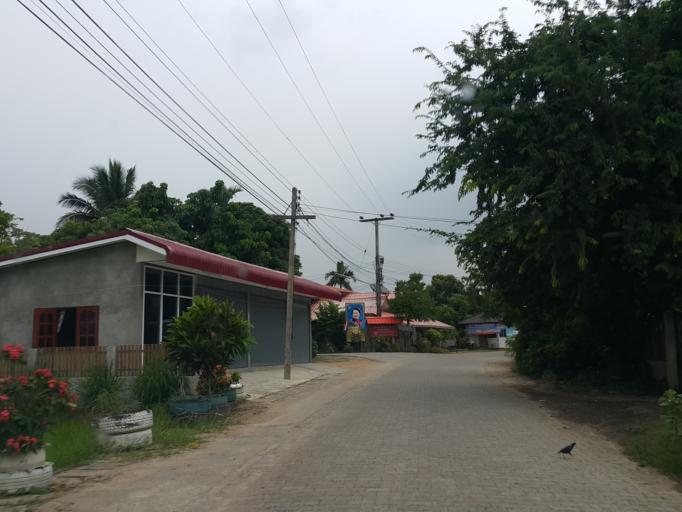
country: TH
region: Chiang Mai
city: Mae On
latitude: 18.7218
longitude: 99.2020
